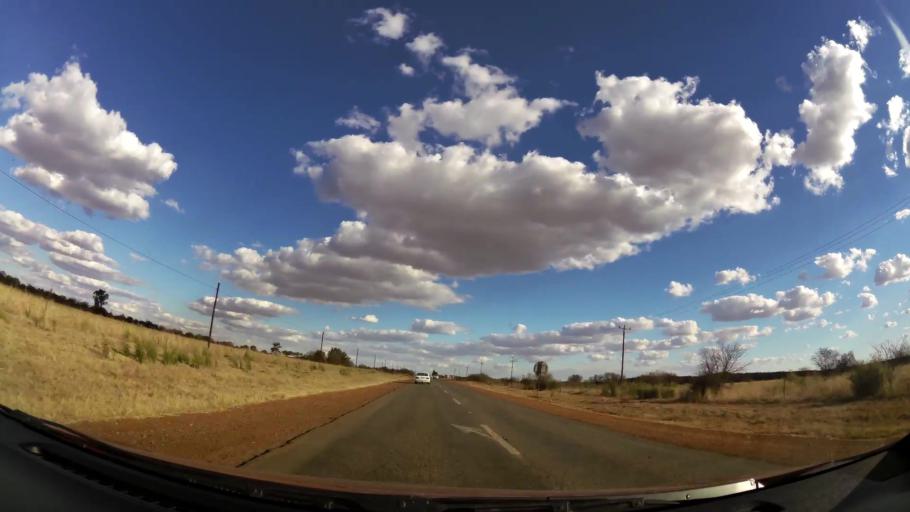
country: ZA
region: North-West
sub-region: Dr Kenneth Kaunda District Municipality
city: Potchefstroom
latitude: -26.5857
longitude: 27.1197
